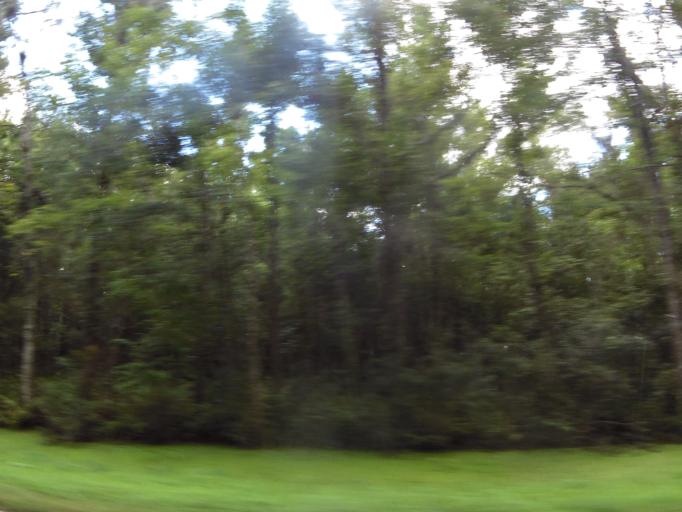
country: US
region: Florida
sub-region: Putnam County
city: East Palatka
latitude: 29.7776
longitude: -81.4864
